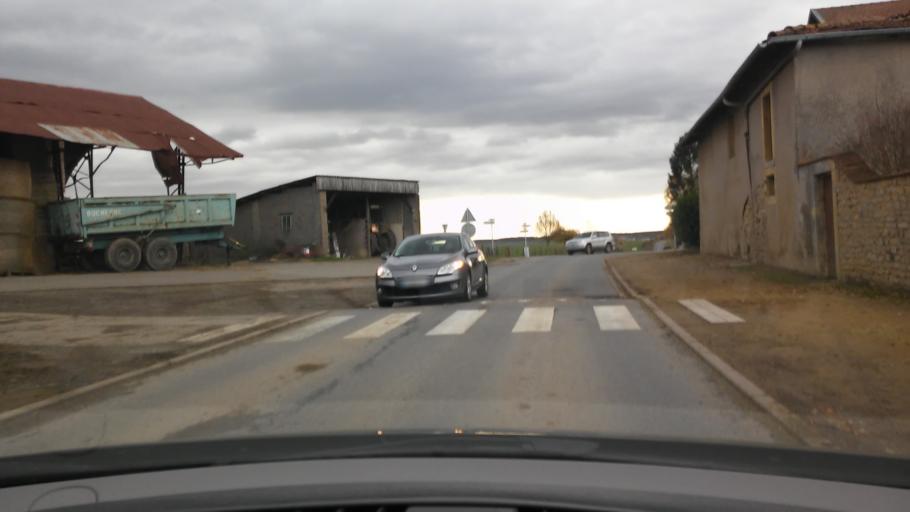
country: FR
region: Lorraine
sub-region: Departement de la Moselle
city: Retonfey
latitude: 49.1605
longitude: 6.3049
